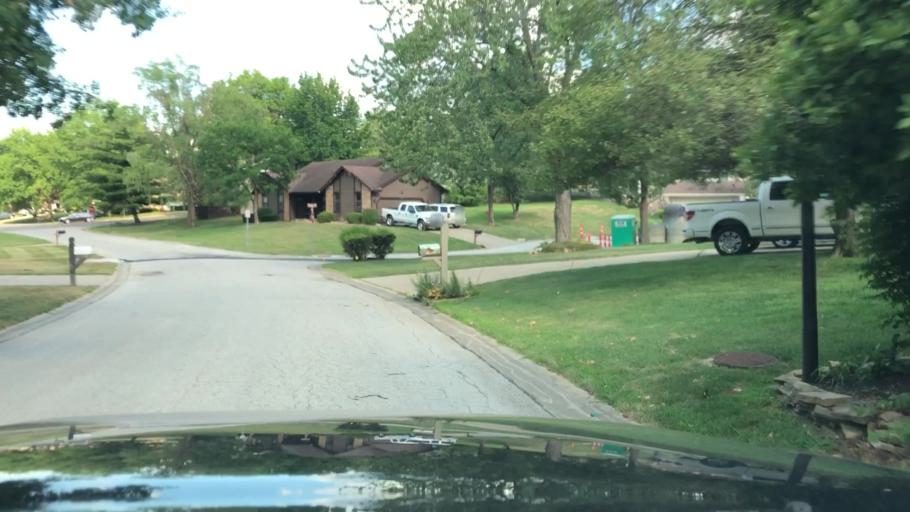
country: US
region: Missouri
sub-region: Saint Charles County
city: Lake Saint Louis
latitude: 38.7961
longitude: -90.8049
